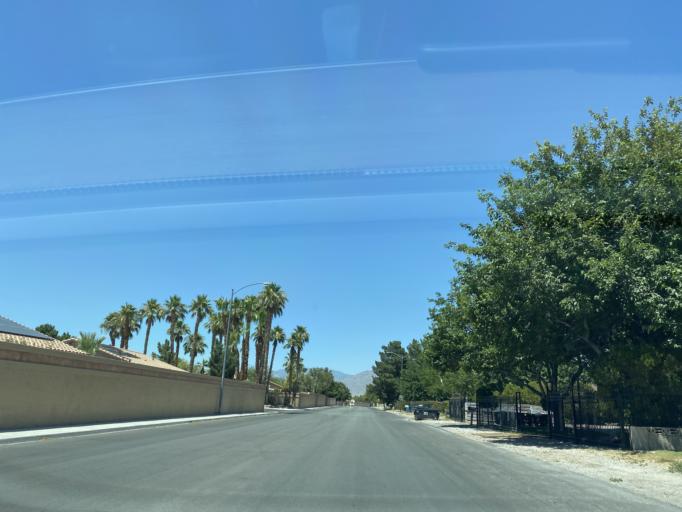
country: US
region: Nevada
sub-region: Clark County
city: Las Vegas
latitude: 36.2285
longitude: -115.2122
